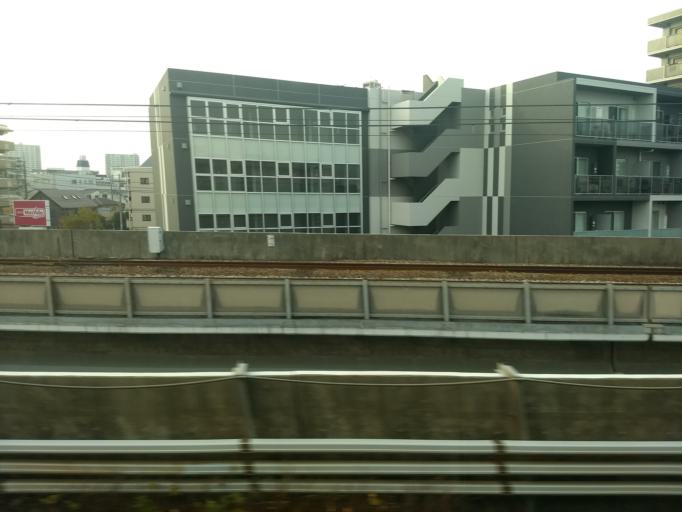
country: JP
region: Kanagawa
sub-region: Kawasaki-shi
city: Kawasaki
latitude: 35.5418
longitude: 139.7072
